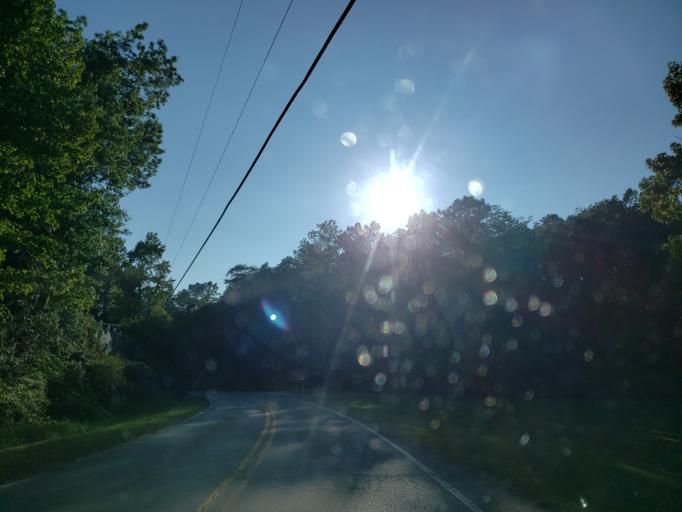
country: US
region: Georgia
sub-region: Bartow County
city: Rydal
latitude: 34.2817
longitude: -84.8080
